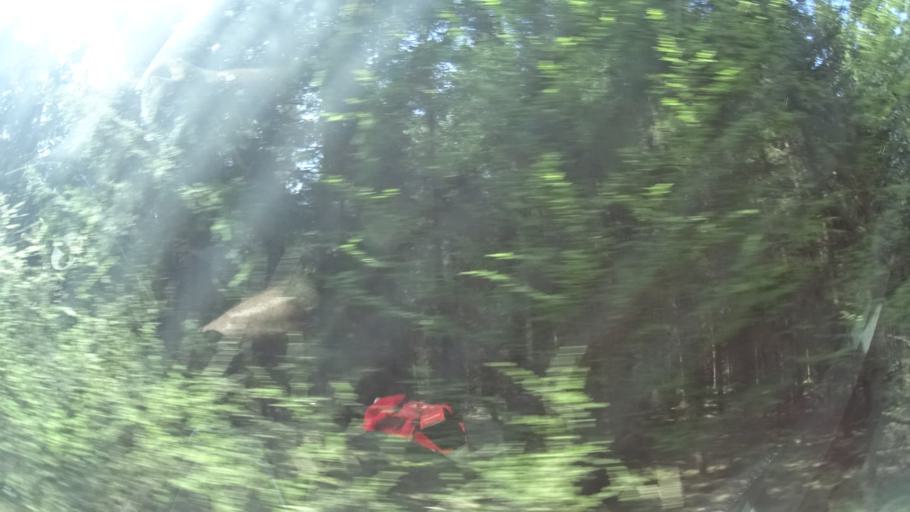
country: DE
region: Thuringia
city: Hellingen
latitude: 50.2801
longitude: 10.7636
